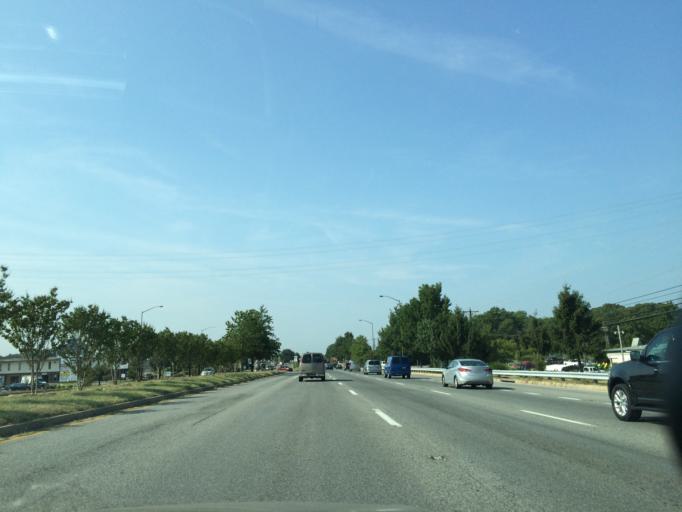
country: US
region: Maryland
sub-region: Charles County
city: Waldorf
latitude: 38.6356
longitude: -76.9014
